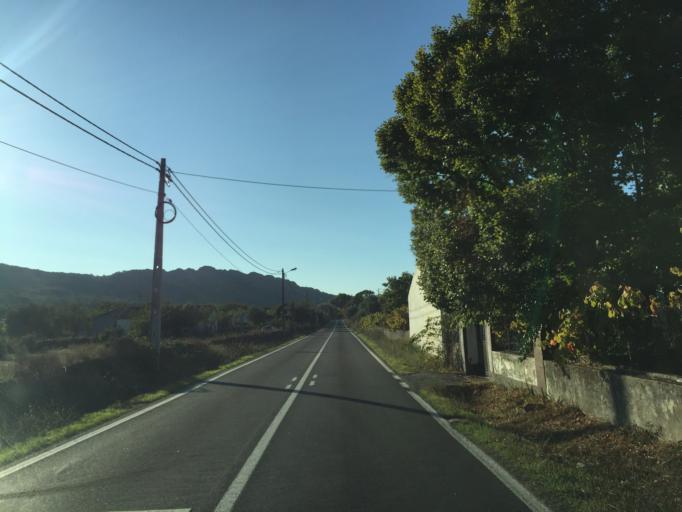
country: PT
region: Portalegre
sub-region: Marvao
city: Marvao
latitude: 39.3865
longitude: -7.4005
